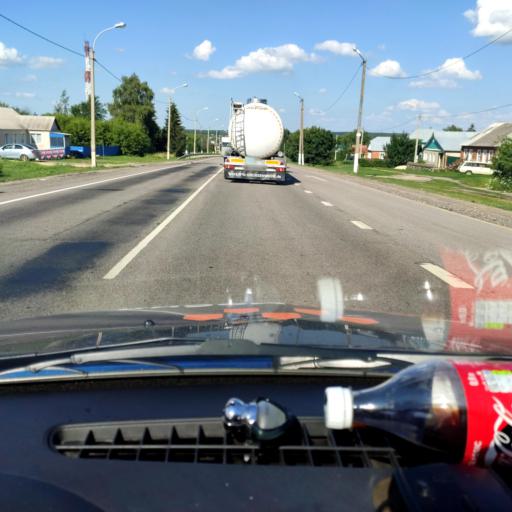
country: RU
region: Lipetsk
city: Kazaki
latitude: 52.6171
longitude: 38.2632
